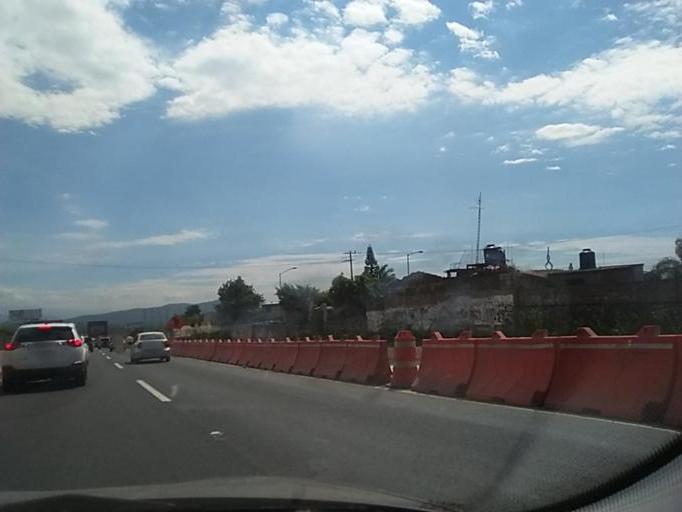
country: MX
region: Morelos
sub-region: Cuernavaca
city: Colonia los Cerritos
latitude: 18.9540
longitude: -99.1958
